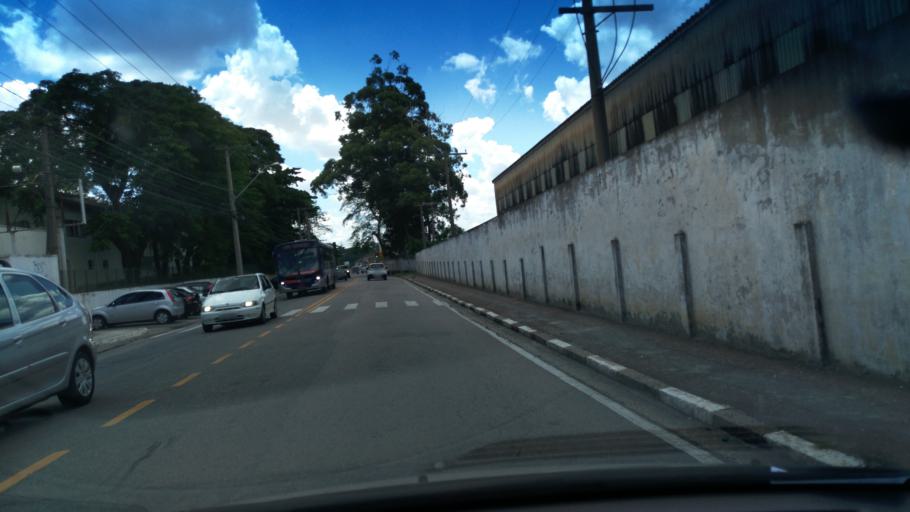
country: BR
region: Sao Paulo
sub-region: Vinhedo
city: Vinhedo
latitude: -23.0152
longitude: -46.9830
